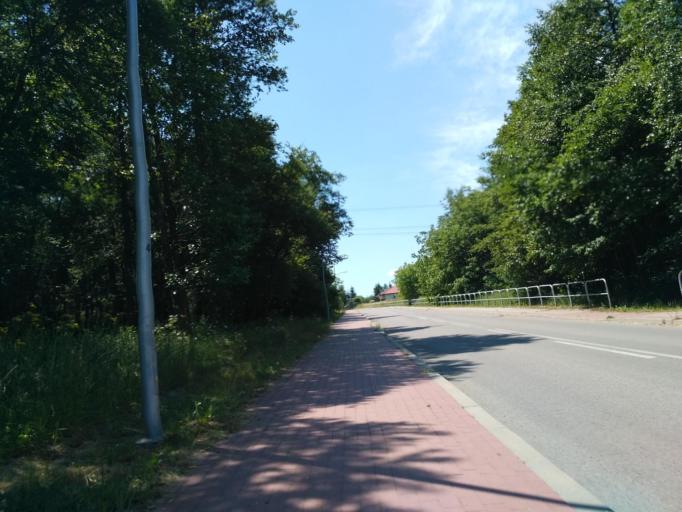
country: PL
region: Subcarpathian Voivodeship
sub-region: Krosno
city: Krosno
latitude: 49.7103
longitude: 21.7825
